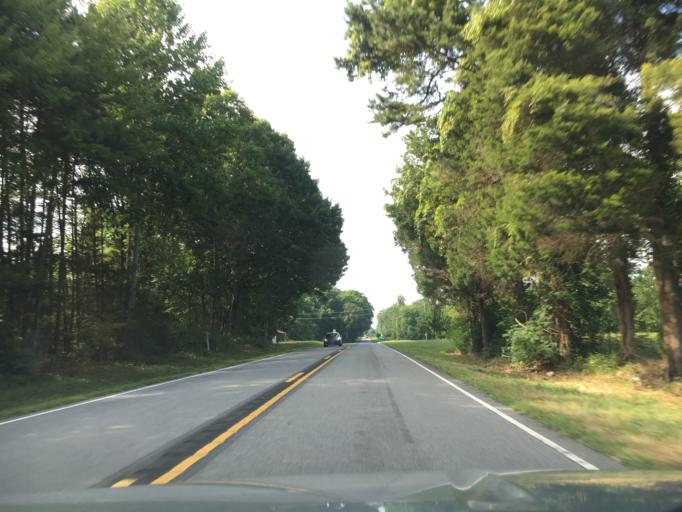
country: US
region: Virginia
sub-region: Halifax County
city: Mountain Road
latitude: 36.8926
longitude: -79.0167
